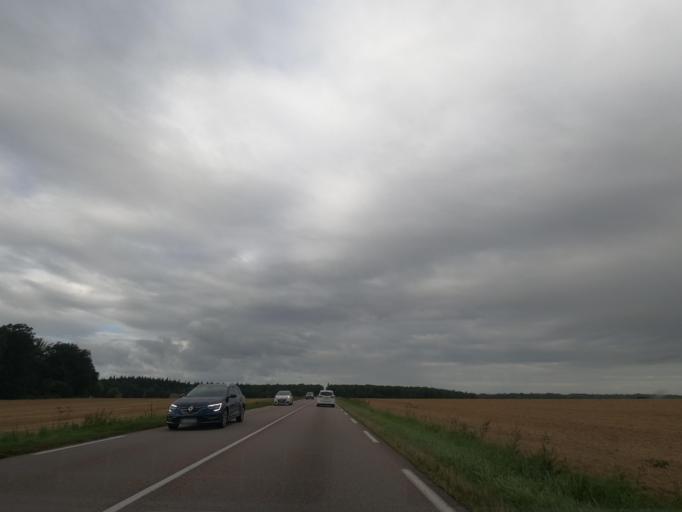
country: FR
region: Haute-Normandie
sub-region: Departement de l'Eure
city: Bourgtheroulde-Infreville
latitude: 49.2740
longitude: 0.8225
